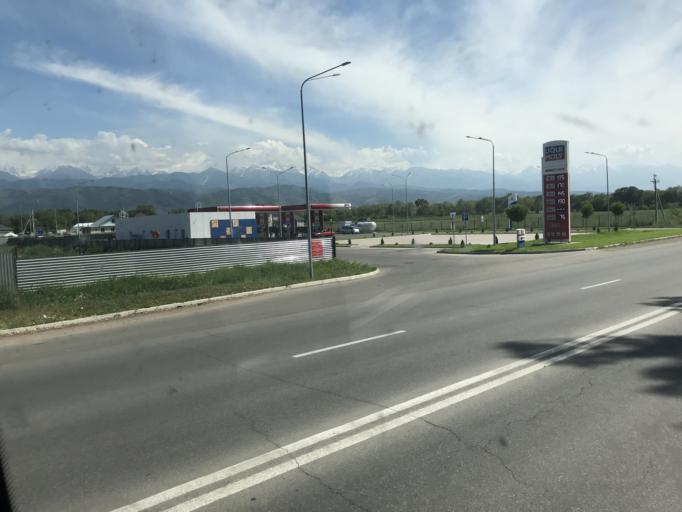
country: KZ
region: Almaty Oblysy
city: Energeticheskiy
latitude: 43.3600
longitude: 77.0769
